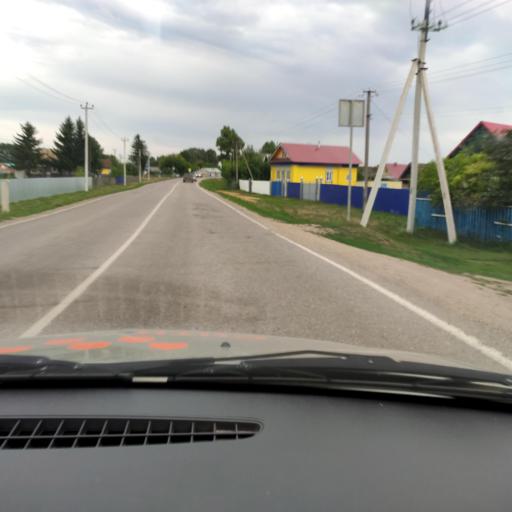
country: RU
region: Bashkortostan
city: Krasnaya Gorka
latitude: 55.1209
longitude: 56.6375
